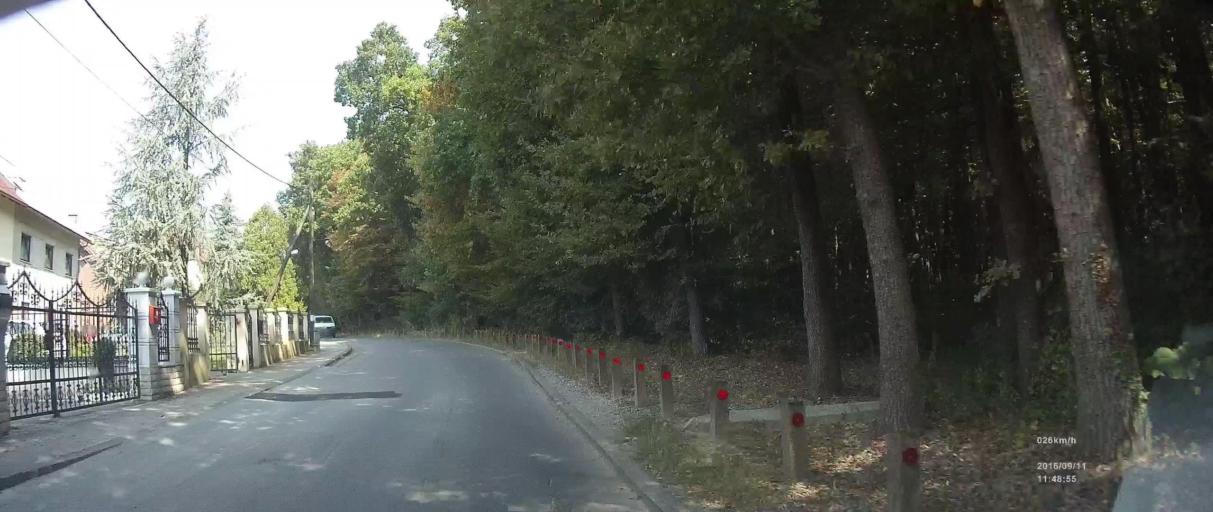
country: HR
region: Grad Zagreb
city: Zagreb
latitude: 45.8320
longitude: 16.0146
